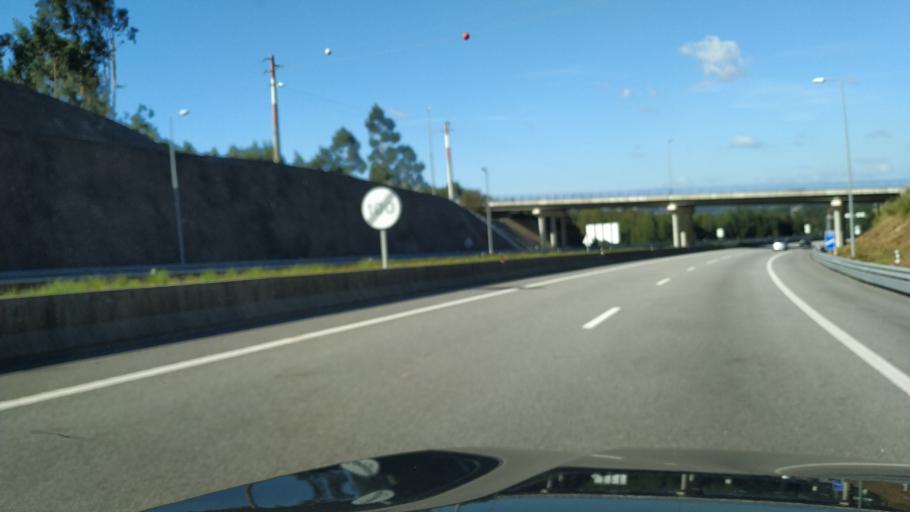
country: PT
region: Porto
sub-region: Vila Nova de Gaia
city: Sandim
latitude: 41.0546
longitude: -8.5198
